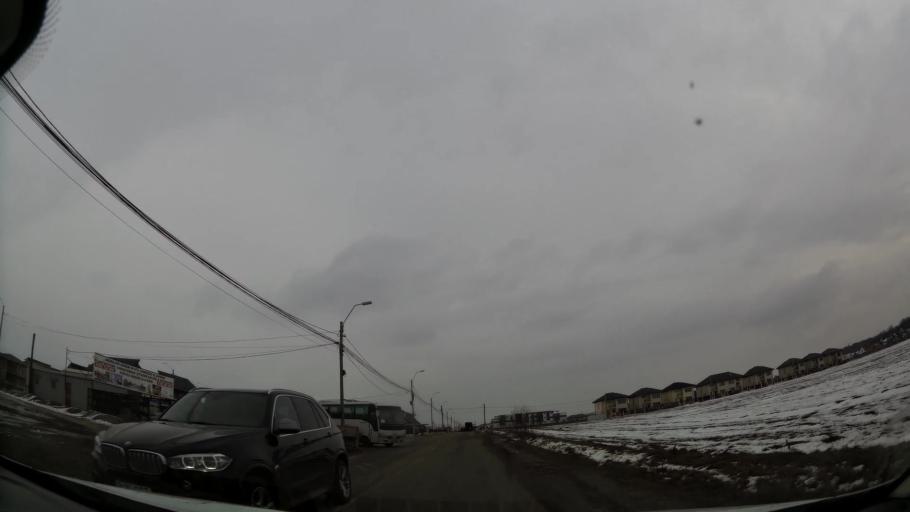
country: RO
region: Ilfov
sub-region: Comuna Tunari
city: Tunari
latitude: 44.5524
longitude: 26.1094
